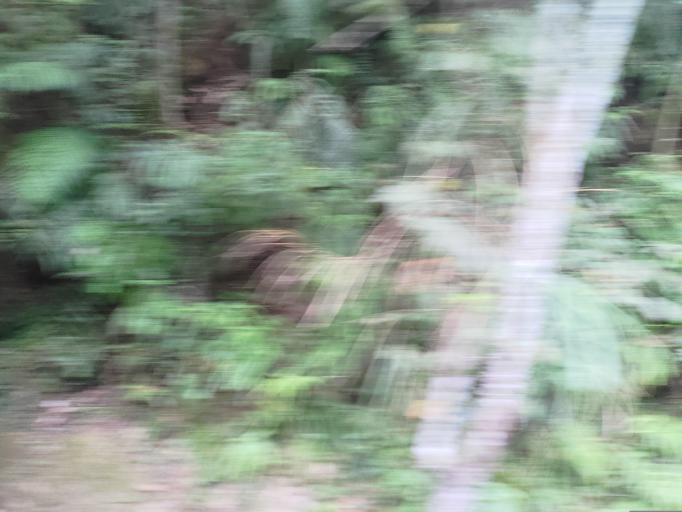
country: TW
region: Taiwan
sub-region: Hsinchu
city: Hsinchu
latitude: 24.6088
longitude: 121.0403
